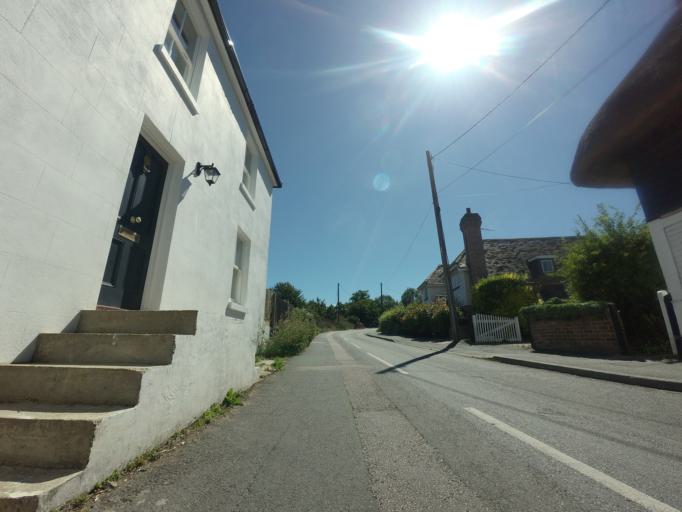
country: GB
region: England
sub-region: Kent
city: Ash
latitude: 51.2778
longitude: 1.2854
